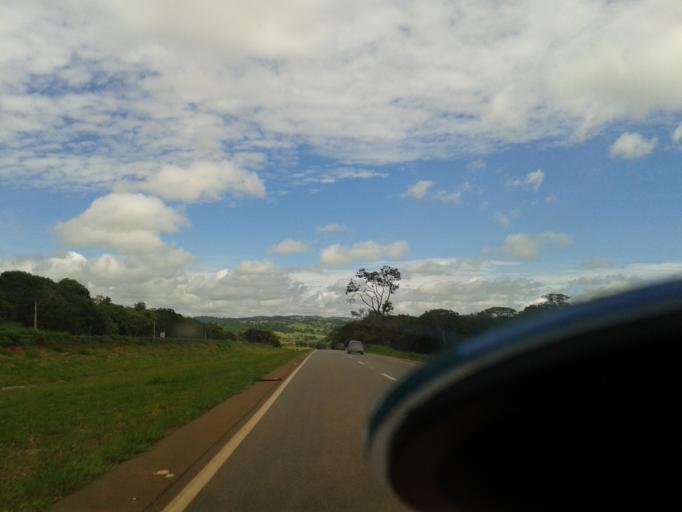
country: BR
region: Goias
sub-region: Inhumas
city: Inhumas
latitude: -16.2390
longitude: -49.5567
